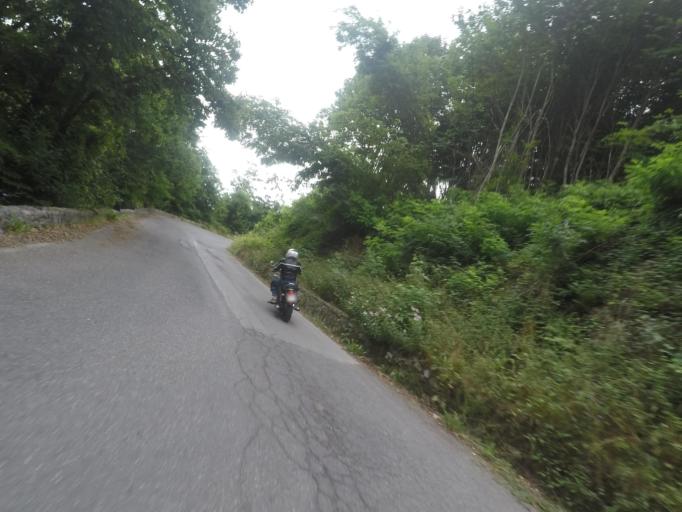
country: IT
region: Tuscany
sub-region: Provincia di Lucca
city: Careggine
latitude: 44.1147
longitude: 10.3618
